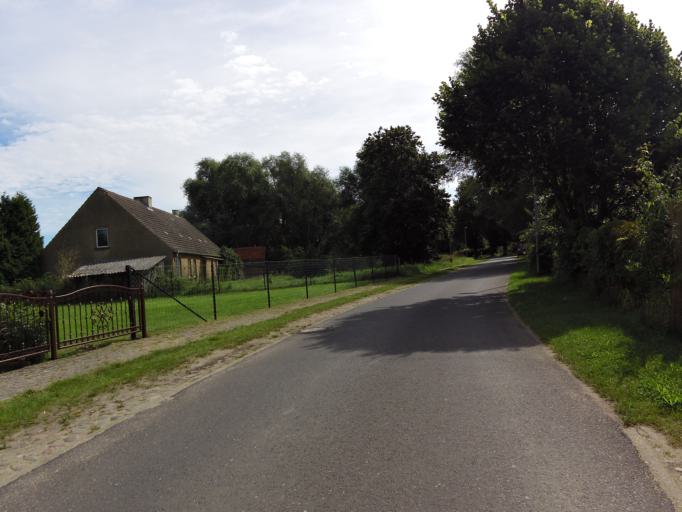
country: DE
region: Brandenburg
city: Lychen
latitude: 53.2900
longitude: 13.3307
